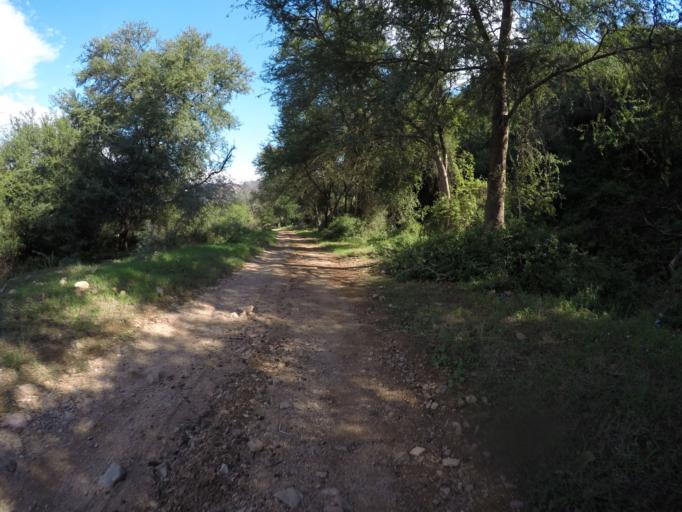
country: ZA
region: Eastern Cape
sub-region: Cacadu District Municipality
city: Kareedouw
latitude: -33.6634
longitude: 24.3900
